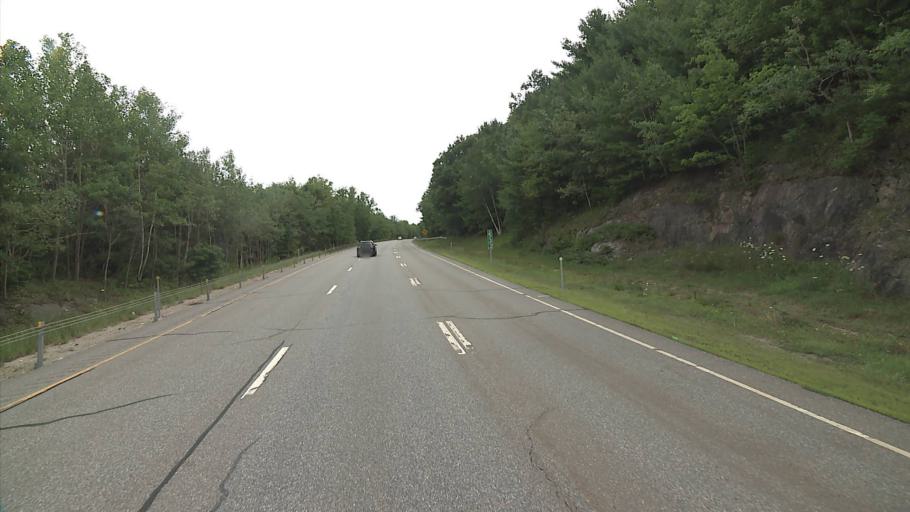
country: US
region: Connecticut
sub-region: Litchfield County
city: Torrington
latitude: 41.8477
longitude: -73.0939
